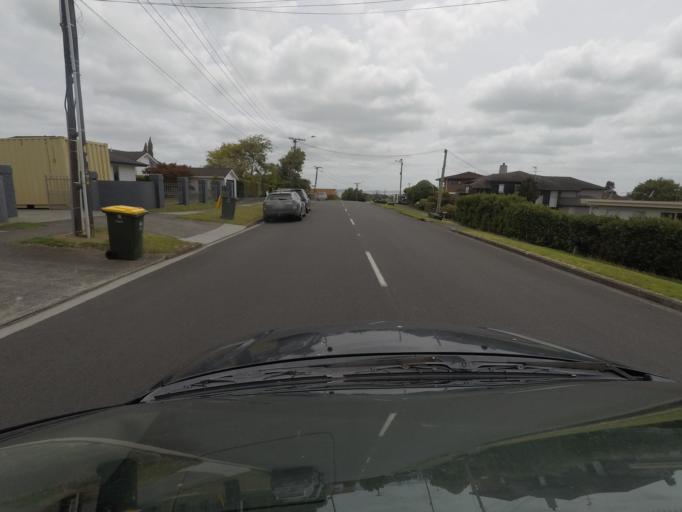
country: NZ
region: Auckland
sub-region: Auckland
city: Pakuranga
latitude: -36.8900
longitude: 174.9306
